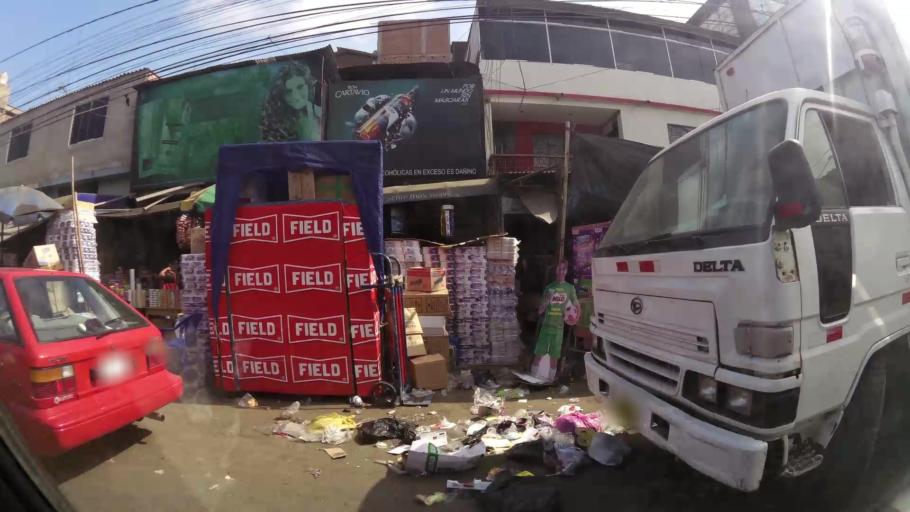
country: PE
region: La Libertad
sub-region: Provincia de Trujillo
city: Trujillo
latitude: -8.1122
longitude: -79.0184
